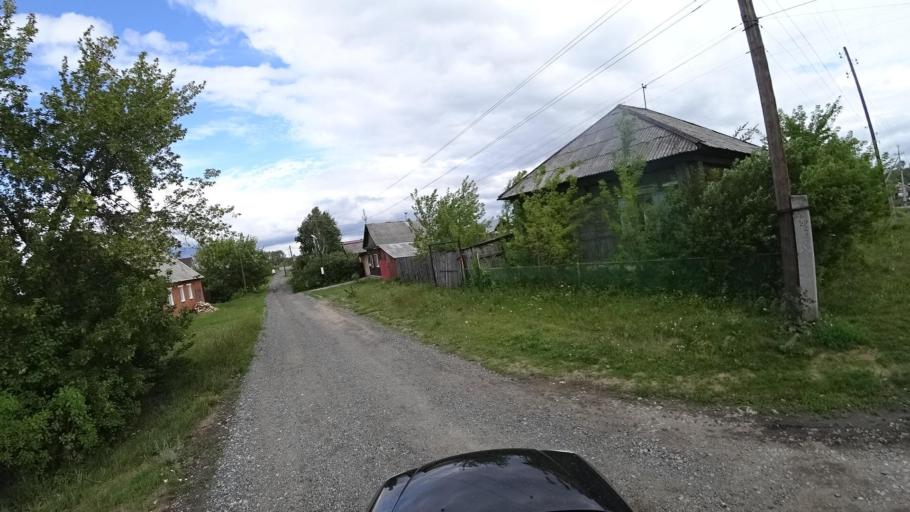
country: RU
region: Sverdlovsk
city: Kamyshlov
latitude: 56.8575
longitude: 62.7002
